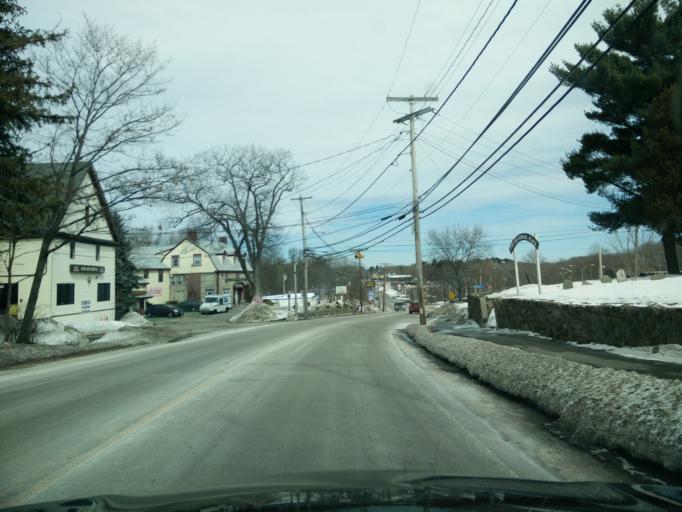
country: US
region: Massachusetts
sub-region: Norfolk County
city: Walpole
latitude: 42.1517
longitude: -71.2489
